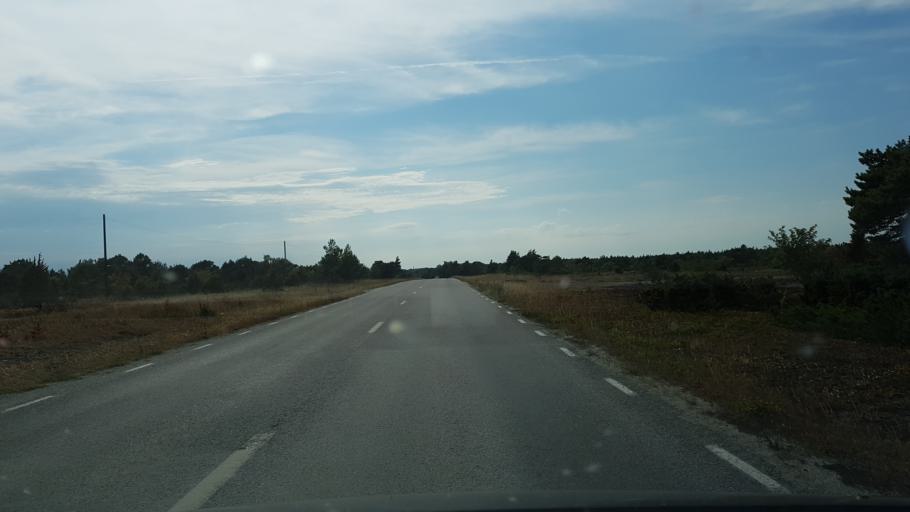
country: SE
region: Gotland
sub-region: Gotland
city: Visby
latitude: 57.6383
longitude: 18.3825
